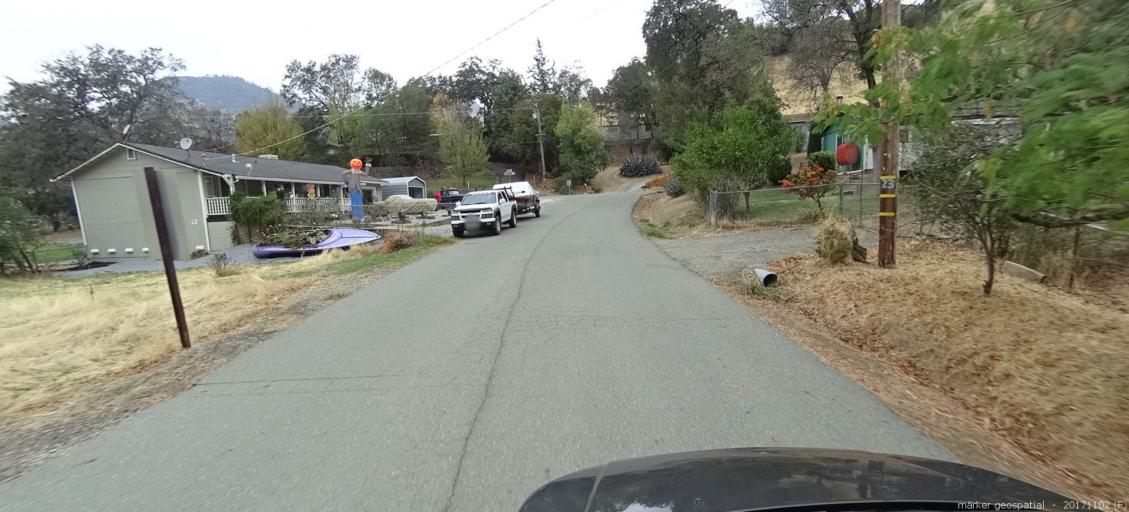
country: US
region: California
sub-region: Shasta County
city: Bella Vista
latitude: 40.7193
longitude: -122.2346
